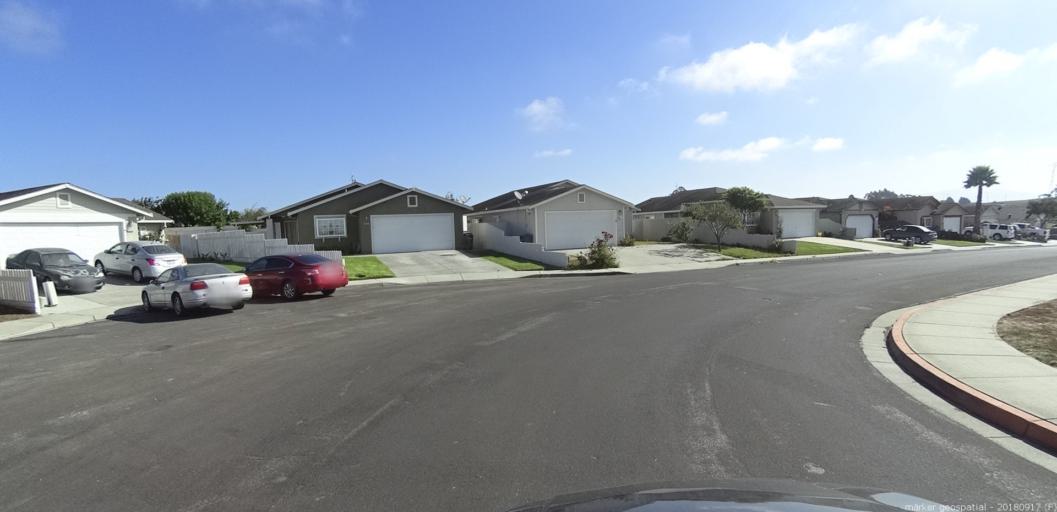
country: US
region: California
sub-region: Monterey County
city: Castroville
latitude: 36.7863
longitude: -121.7288
